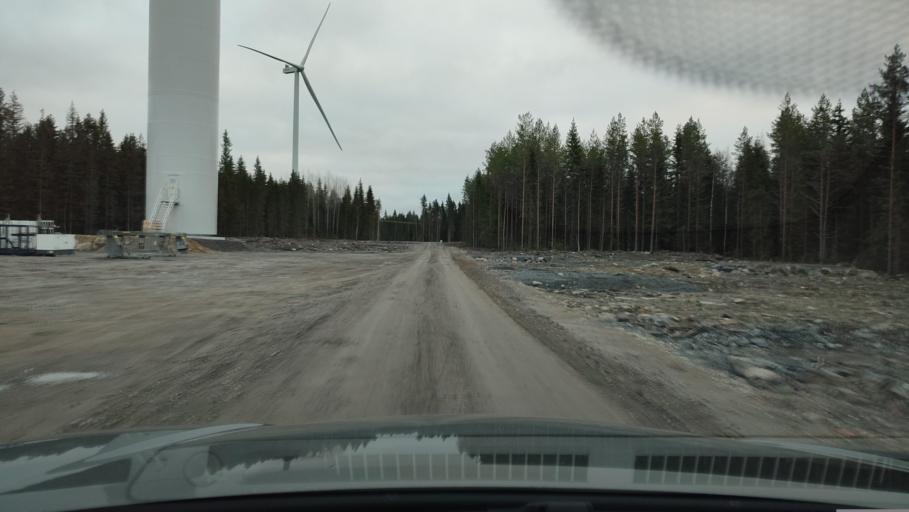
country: FI
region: Southern Ostrobothnia
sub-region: Suupohja
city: Karijoki
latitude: 62.1892
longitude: 21.5838
